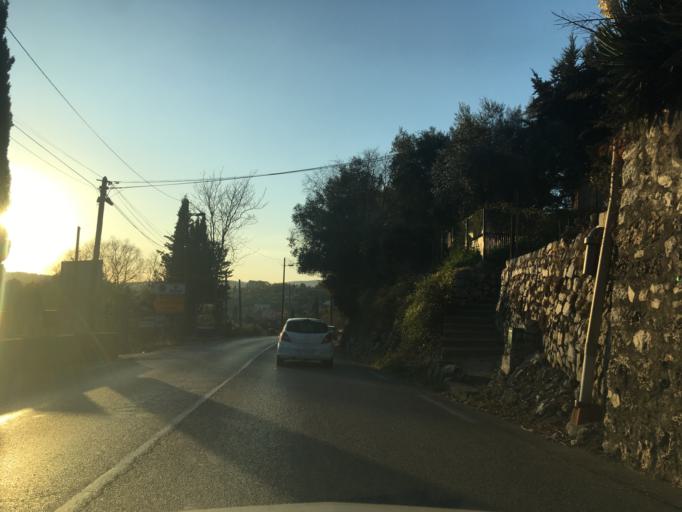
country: FR
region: Provence-Alpes-Cote d'Azur
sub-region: Departement des Alpes-Maritimes
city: Grasse
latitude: 43.6432
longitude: 6.9050
